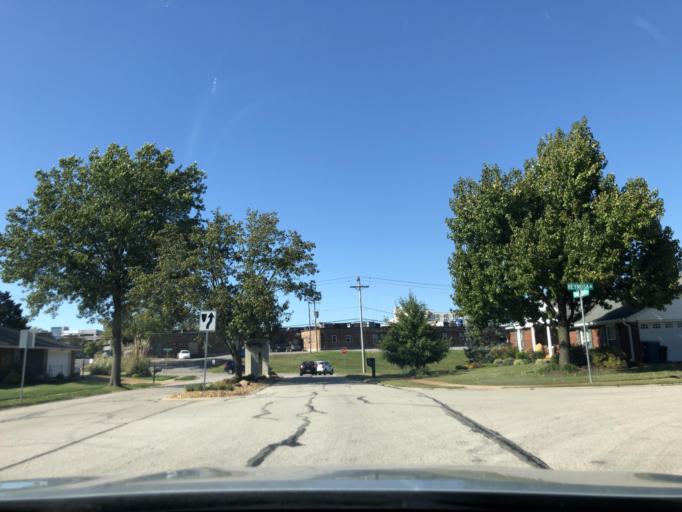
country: US
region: Missouri
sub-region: Saint Louis County
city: Concord
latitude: 38.5035
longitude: -90.3768
